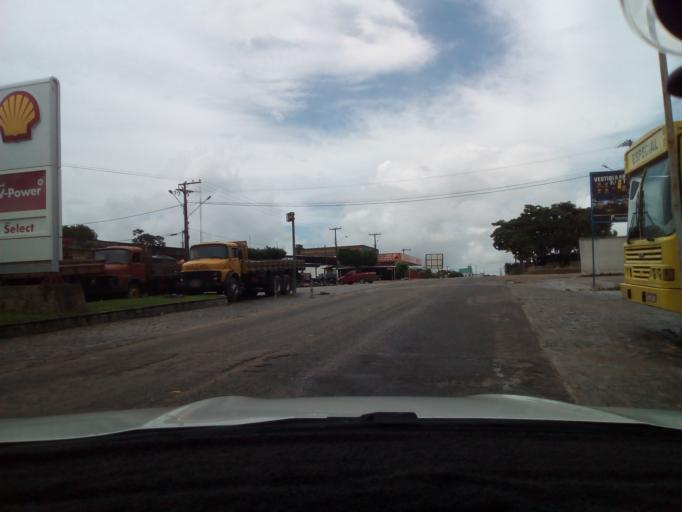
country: BR
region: Paraiba
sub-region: Pedras De Fogo
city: Pedras de Fogo
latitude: -7.4042
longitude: -35.1229
